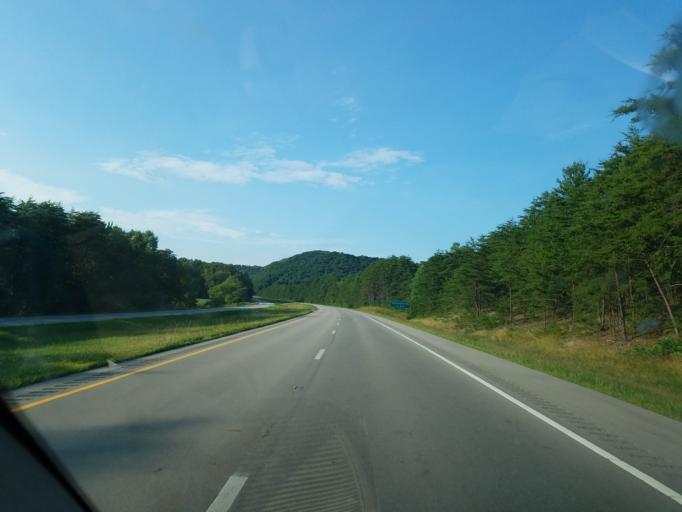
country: US
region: Ohio
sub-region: Adams County
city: Peebles
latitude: 39.0007
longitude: -83.2987
